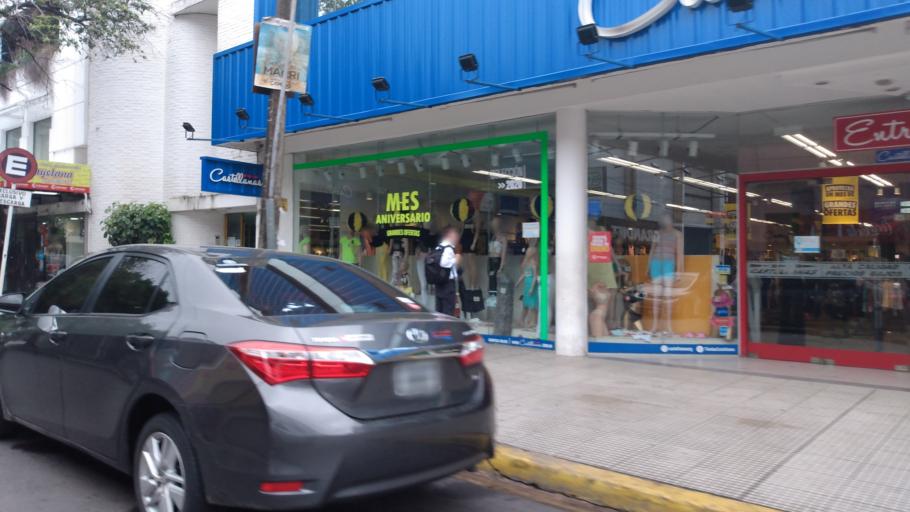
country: AR
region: Corrientes
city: Corrientes
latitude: -27.4677
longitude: -58.8318
